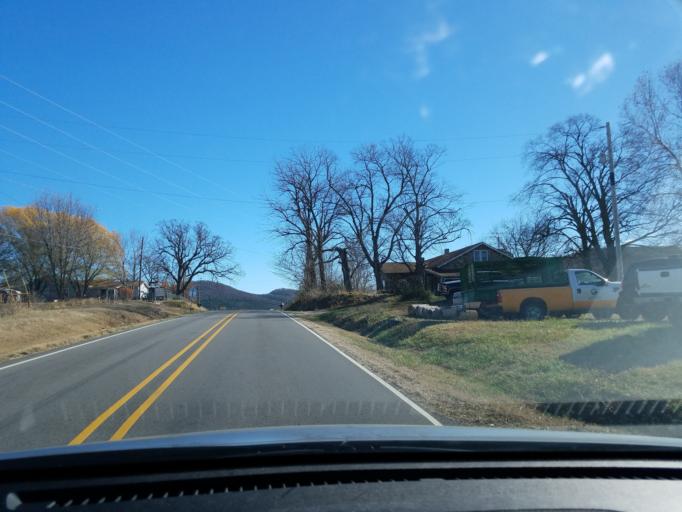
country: US
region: Arkansas
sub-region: Carroll County
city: Berryville
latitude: 36.3924
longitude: -93.5635
